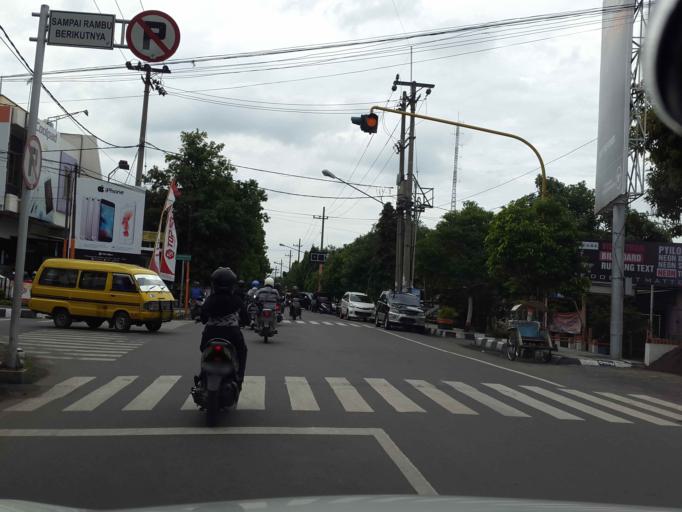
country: ID
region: East Java
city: Mojokerto
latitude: -7.4719
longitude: 112.4364
